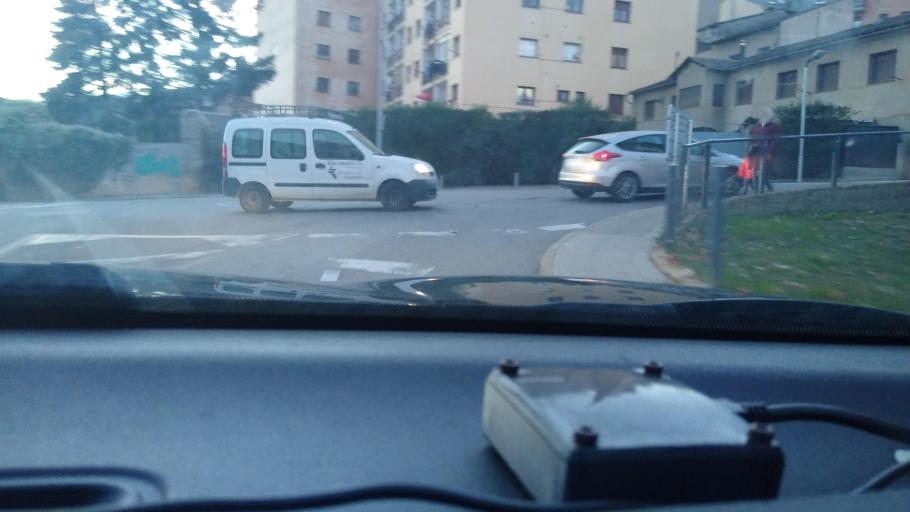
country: ES
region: Catalonia
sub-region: Provincia de Girona
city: Puigcerda
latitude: 42.4299
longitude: 1.9299
